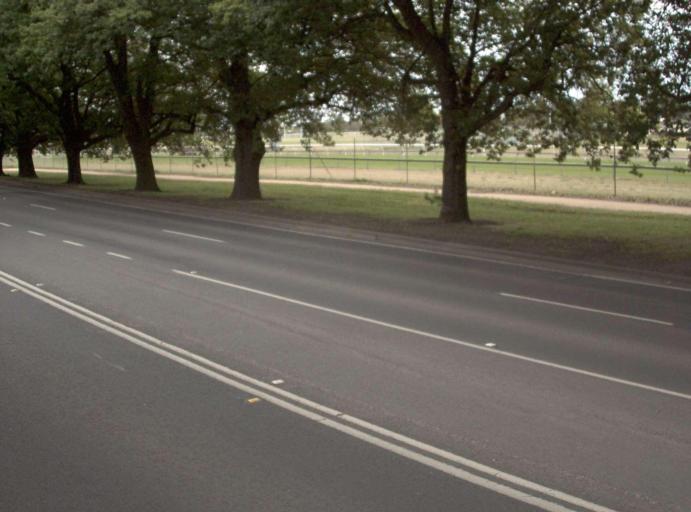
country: AU
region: Victoria
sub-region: Casey
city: Cranbourne
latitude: -38.1151
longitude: 145.2846
